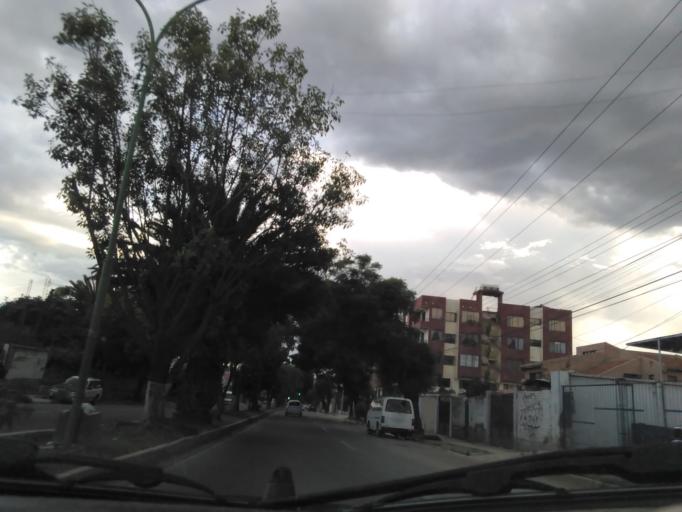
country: BO
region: Cochabamba
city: Cochabamba
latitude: -17.3742
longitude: -66.1758
